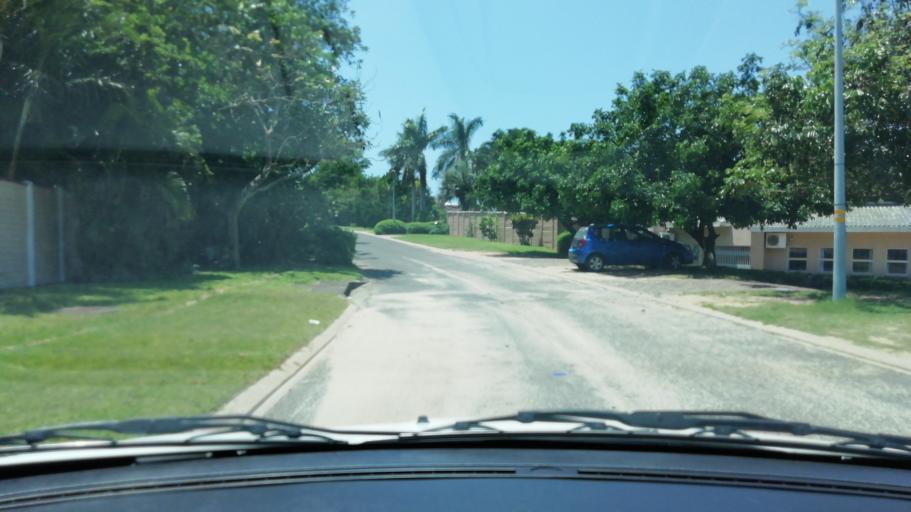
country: ZA
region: KwaZulu-Natal
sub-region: uThungulu District Municipality
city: Richards Bay
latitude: -28.7378
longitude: 32.0629
